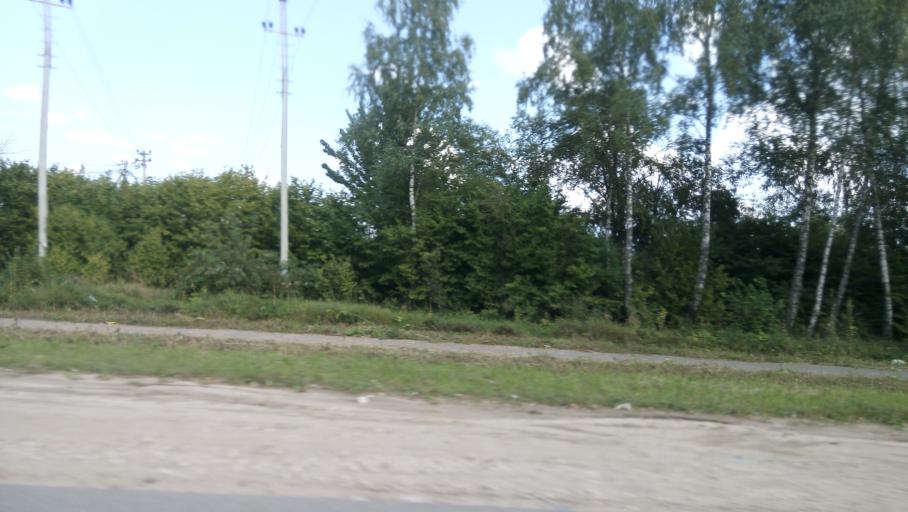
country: RU
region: Moskovskaya
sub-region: Chekhovskiy Rayon
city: Chekhov
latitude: 55.1216
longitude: 37.4491
